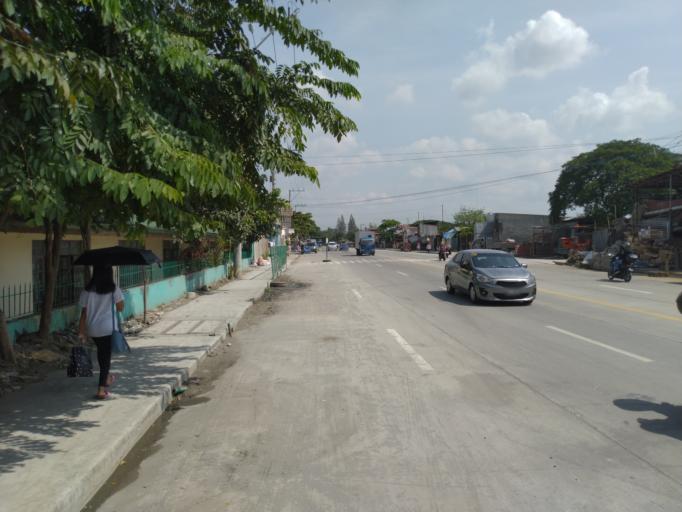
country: PH
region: Calabarzon
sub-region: Province of Rizal
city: Taytay
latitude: 14.5377
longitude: 121.1121
